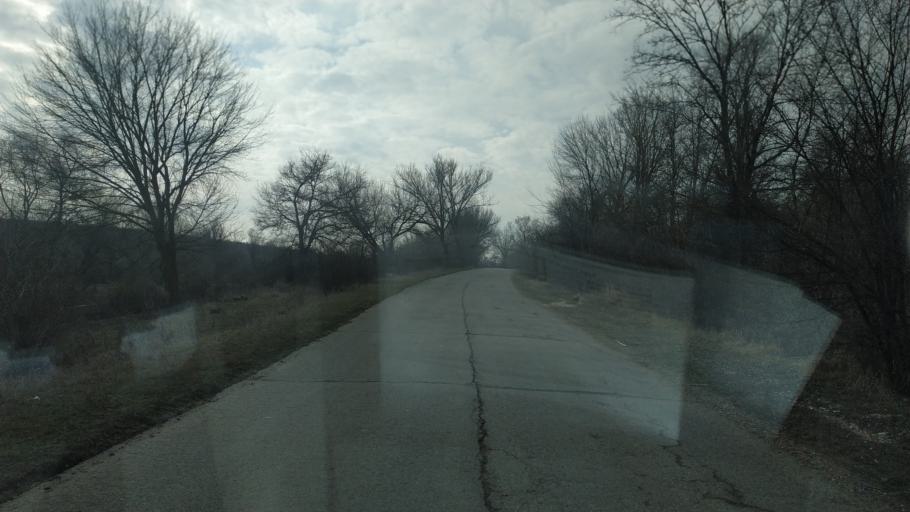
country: MD
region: Chisinau
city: Vadul lui Voda
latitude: 47.0032
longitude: 29.1119
